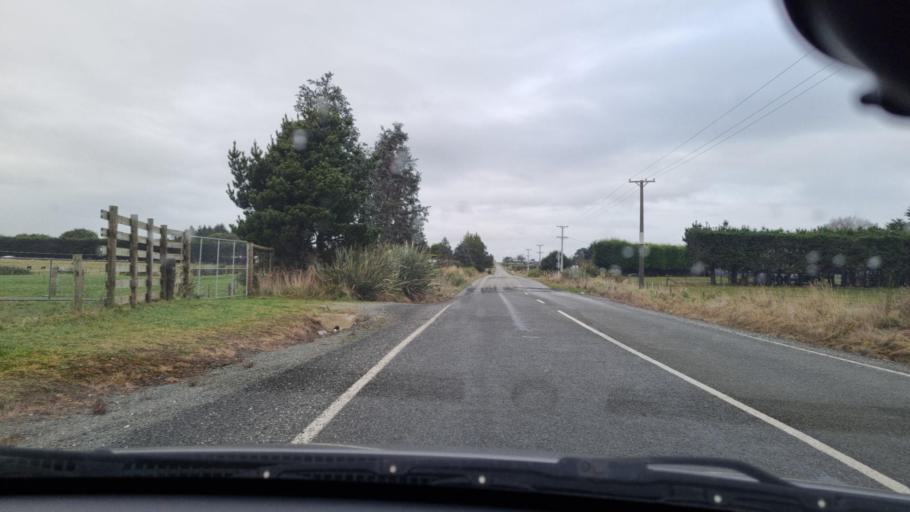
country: NZ
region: Southland
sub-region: Invercargill City
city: Invercargill
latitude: -46.4506
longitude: 168.3809
